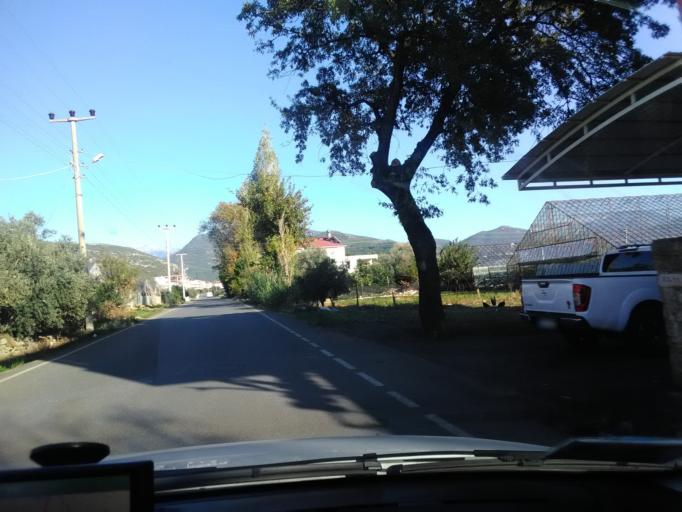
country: TR
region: Antalya
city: Gazipasa
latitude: 36.2716
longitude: 32.3331
